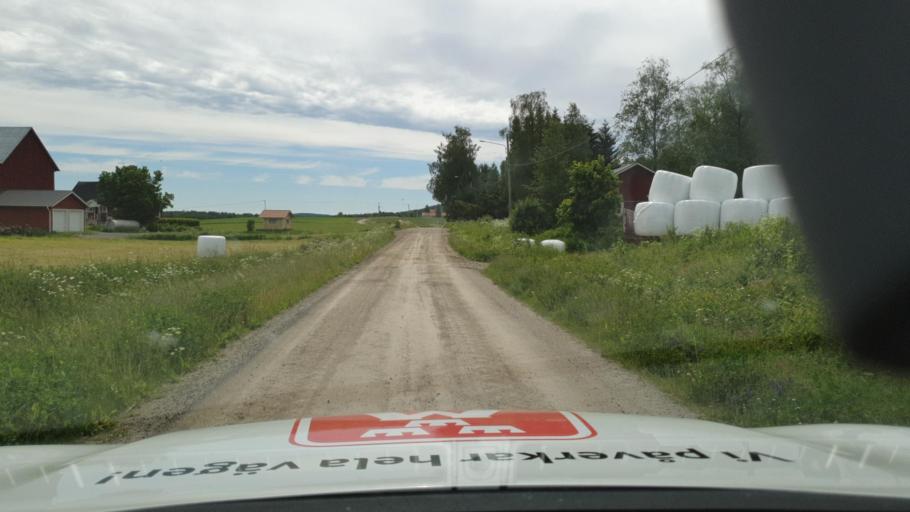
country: SE
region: Vaesterbotten
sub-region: Robertsfors Kommun
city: Robertsfors
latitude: 64.2727
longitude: 20.6266
